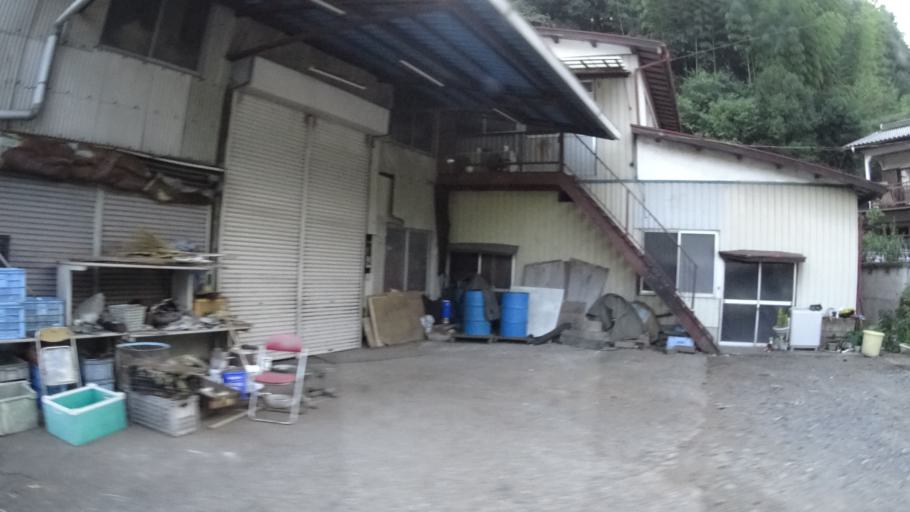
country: JP
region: Tochigi
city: Karasuyama
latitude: 36.6013
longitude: 140.1510
